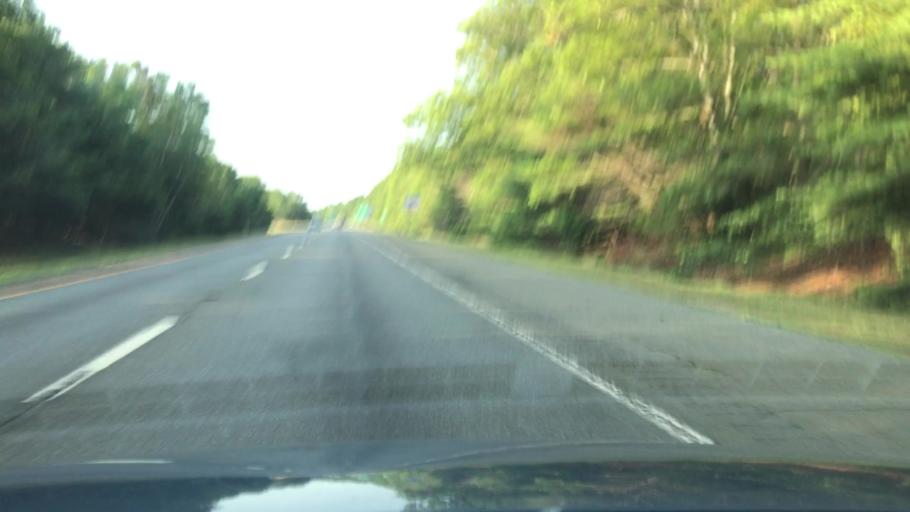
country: US
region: Massachusetts
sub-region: Plymouth County
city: Kingston
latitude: 42.0346
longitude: -70.7249
